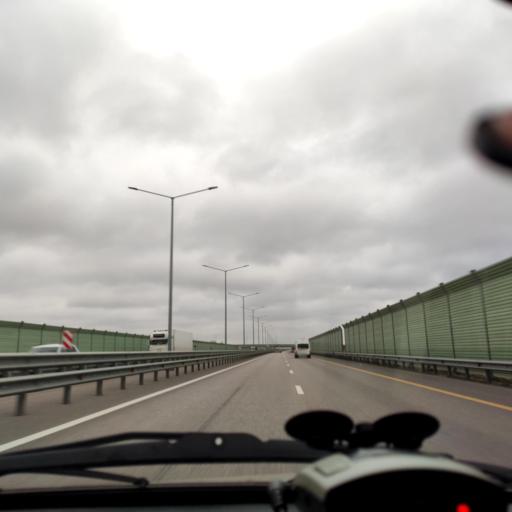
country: RU
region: Voronezj
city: Novaya Usman'
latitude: 51.6045
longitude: 39.3320
